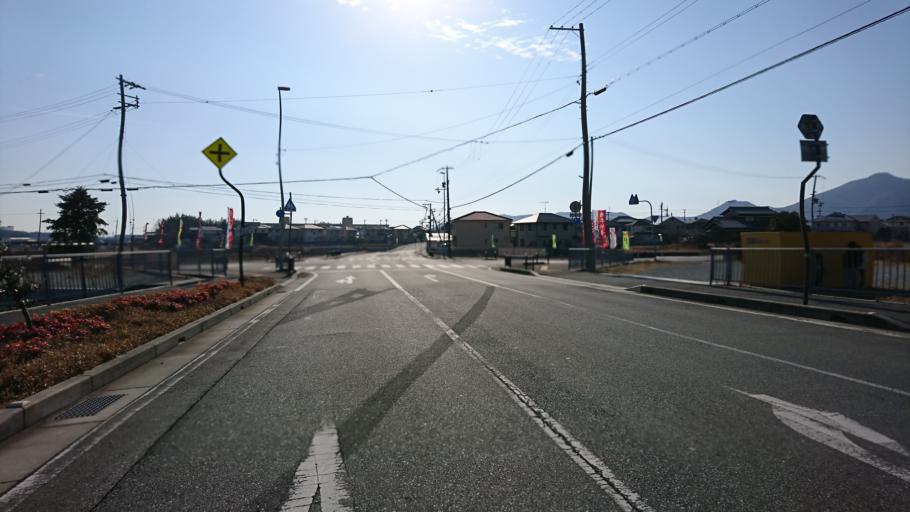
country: JP
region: Hyogo
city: Kakogawacho-honmachi
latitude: 34.8223
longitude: 134.8242
